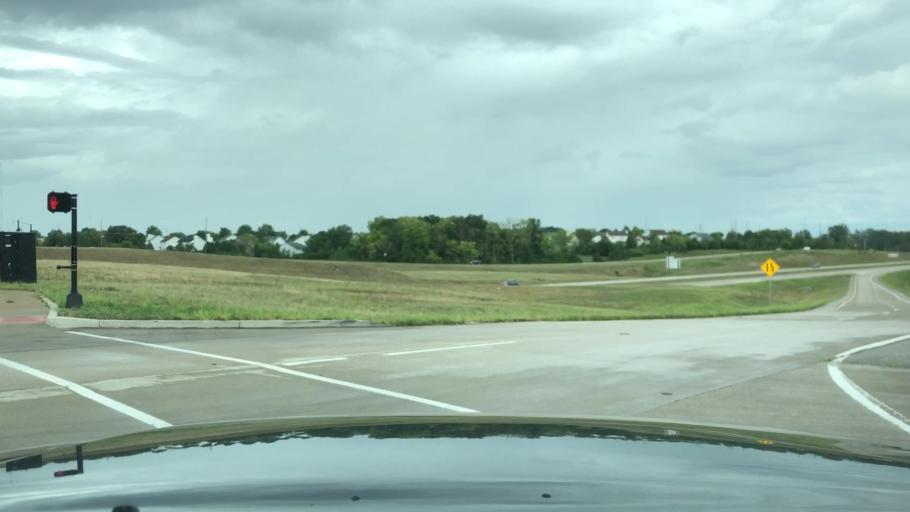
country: US
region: Missouri
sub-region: Saint Charles County
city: Dardenne Prairie
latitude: 38.7675
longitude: -90.7427
